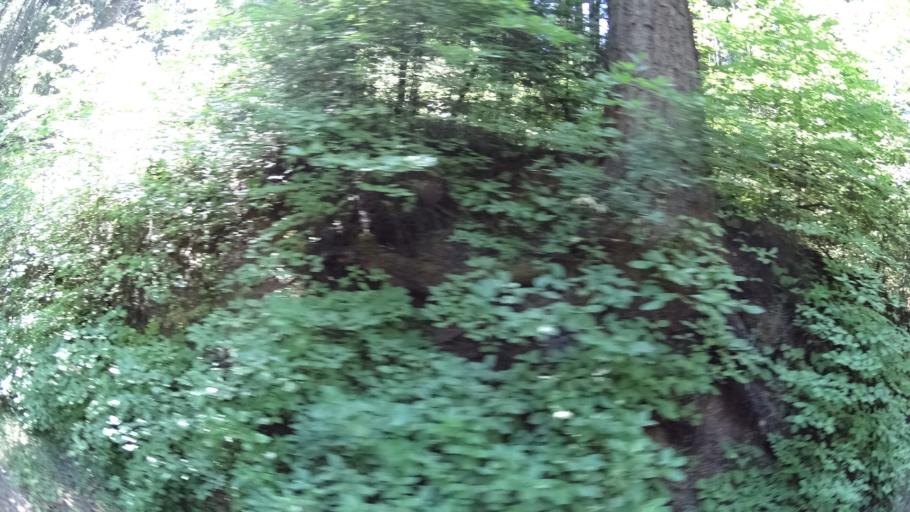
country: US
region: California
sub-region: Calaveras County
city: Arnold
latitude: 38.2457
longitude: -120.3317
